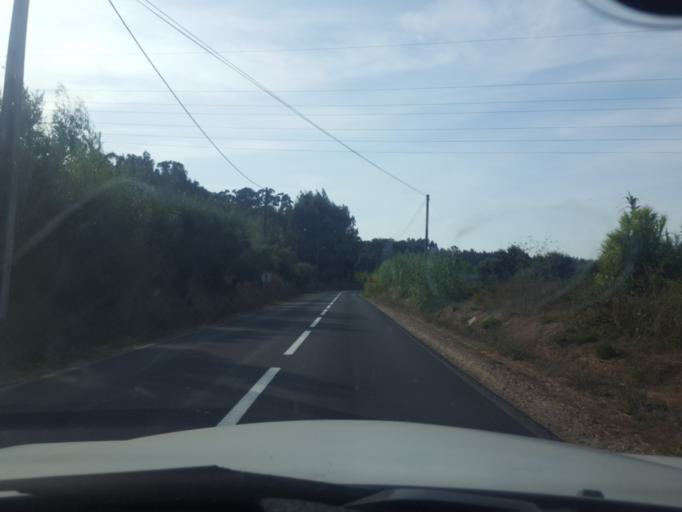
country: PT
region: Leiria
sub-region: Leiria
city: Leiria
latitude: 39.7194
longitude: -8.7907
